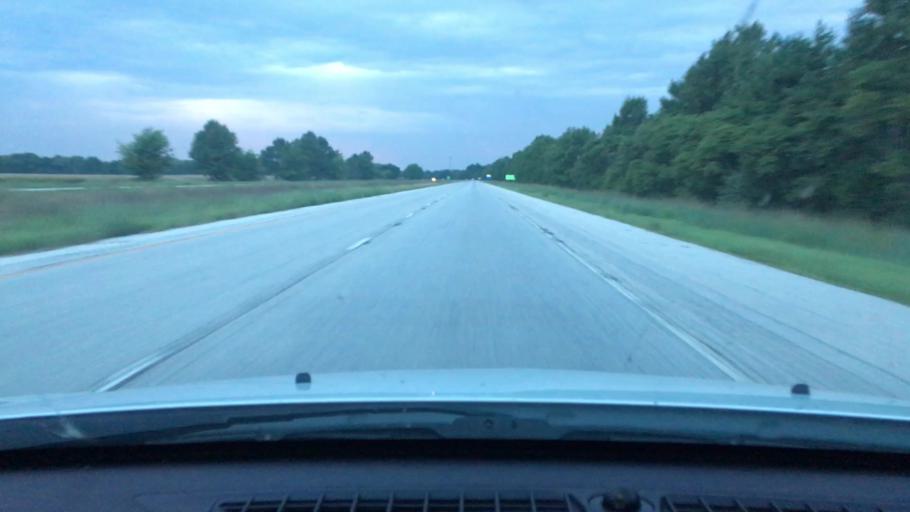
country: US
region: Illinois
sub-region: Morgan County
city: Jacksonville
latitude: 39.7379
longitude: -90.1350
